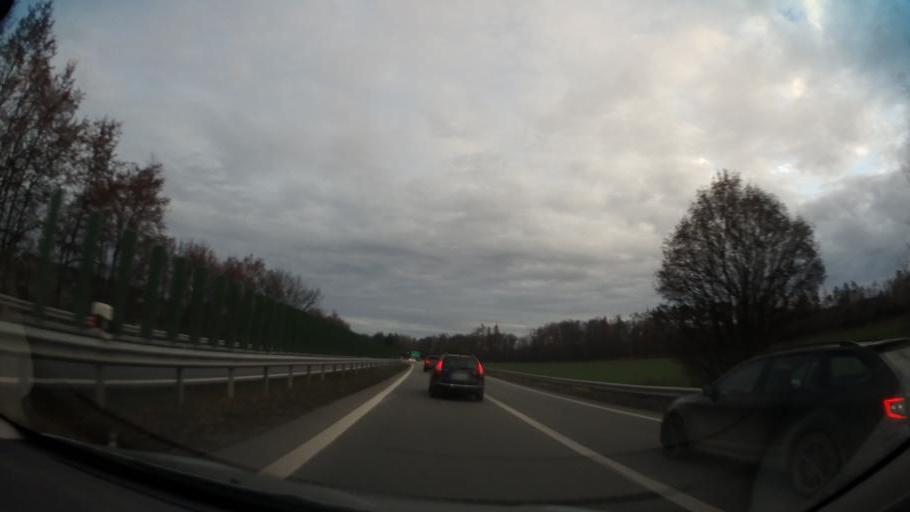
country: CZ
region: South Moravian
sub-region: Okres Brno-Venkov
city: Rosice
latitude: 49.1912
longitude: 16.4330
